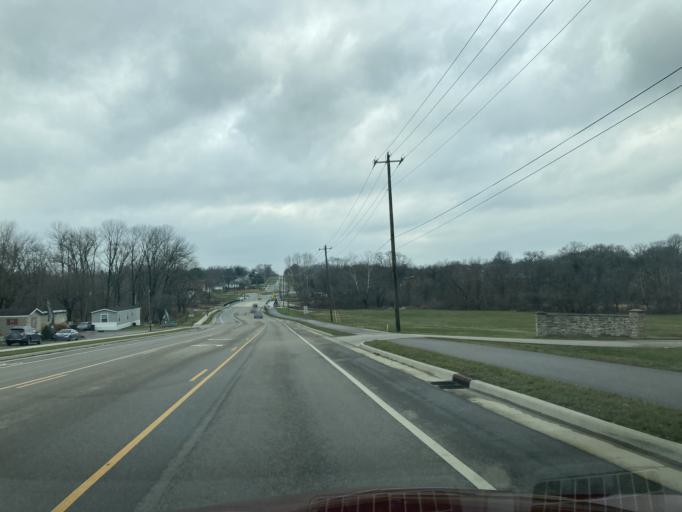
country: US
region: Indiana
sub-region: Monroe County
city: Bloomington
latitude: 39.1215
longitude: -86.5342
